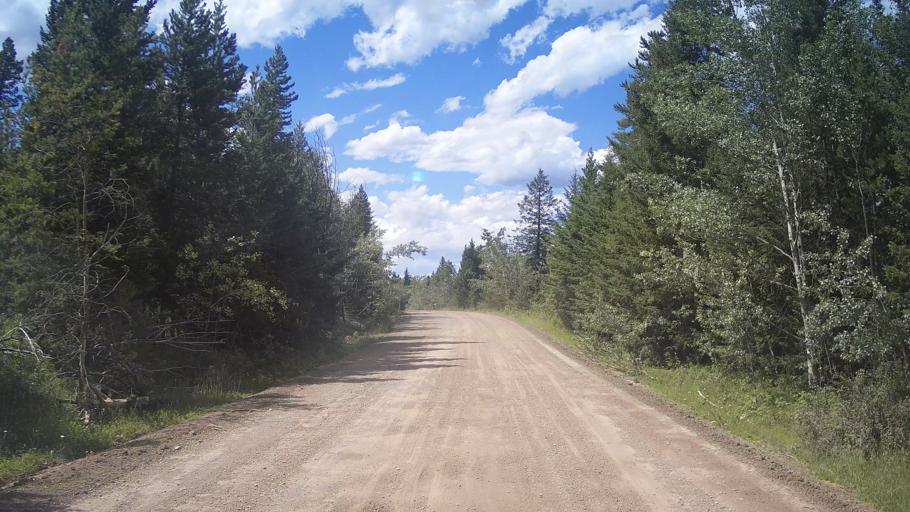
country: CA
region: British Columbia
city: Lillooet
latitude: 51.3281
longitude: -121.8870
